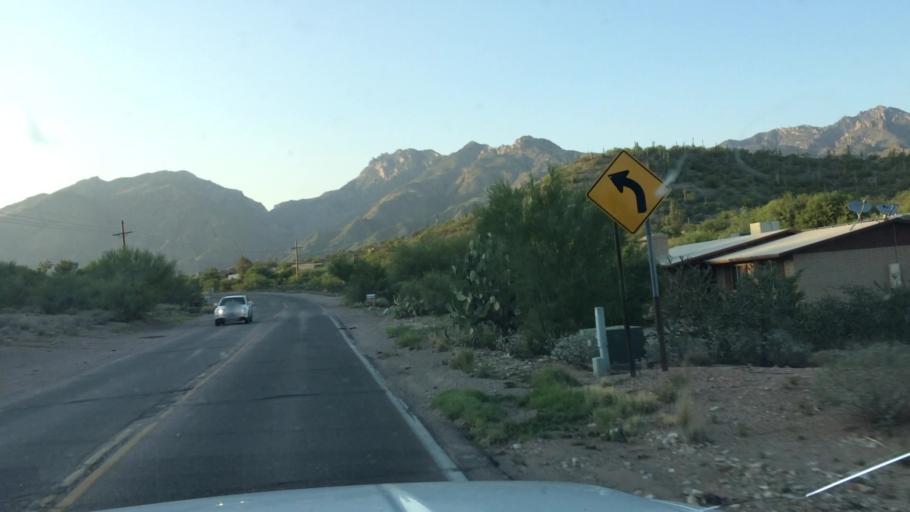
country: US
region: Arizona
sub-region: Pima County
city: Catalina Foothills
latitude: 32.3008
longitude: -110.8405
